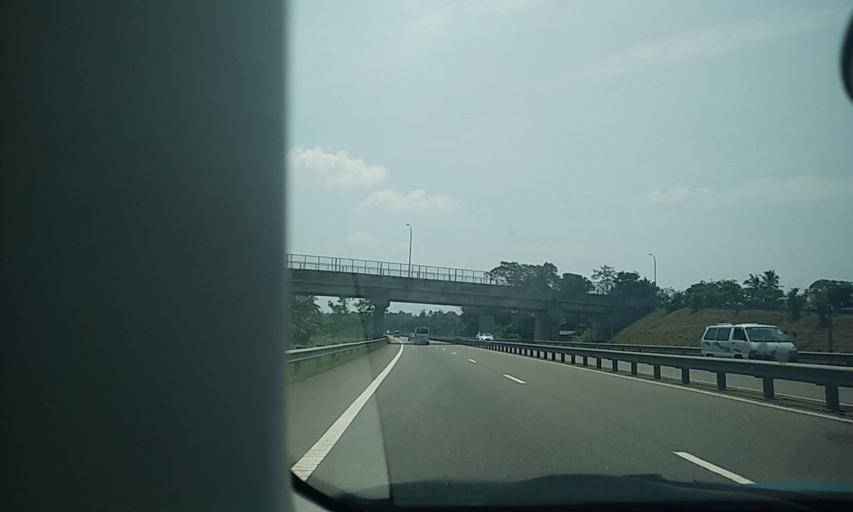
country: LK
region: Western
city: Homagama
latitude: 6.7740
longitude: 79.9810
